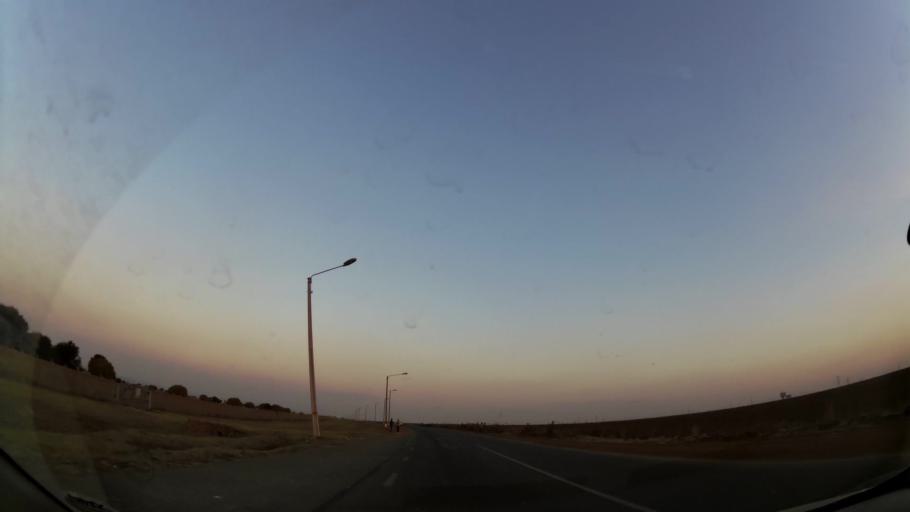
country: ZA
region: Gauteng
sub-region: Ekurhuleni Metropolitan Municipality
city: Nigel
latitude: -26.3552
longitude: 28.4134
